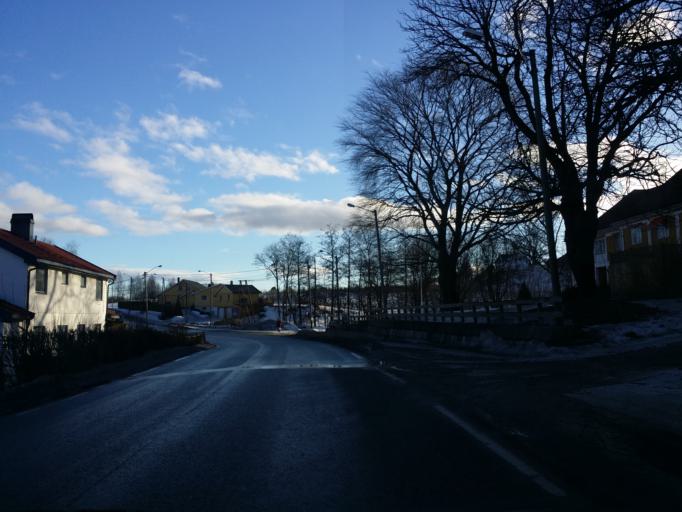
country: NO
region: Buskerud
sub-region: Lier
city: Lierbyen
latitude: 59.8115
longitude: 10.2198
